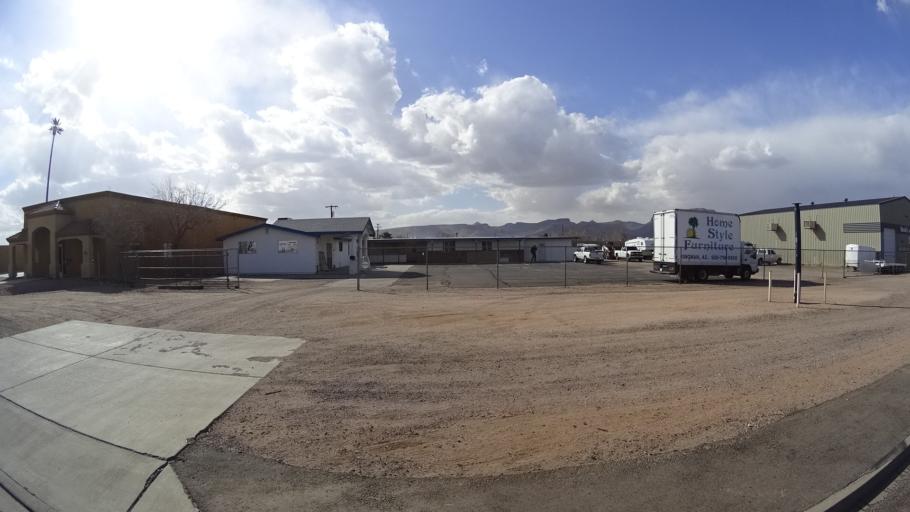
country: US
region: Arizona
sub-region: Mohave County
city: New Kingman-Butler
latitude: 35.2407
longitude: -114.0118
